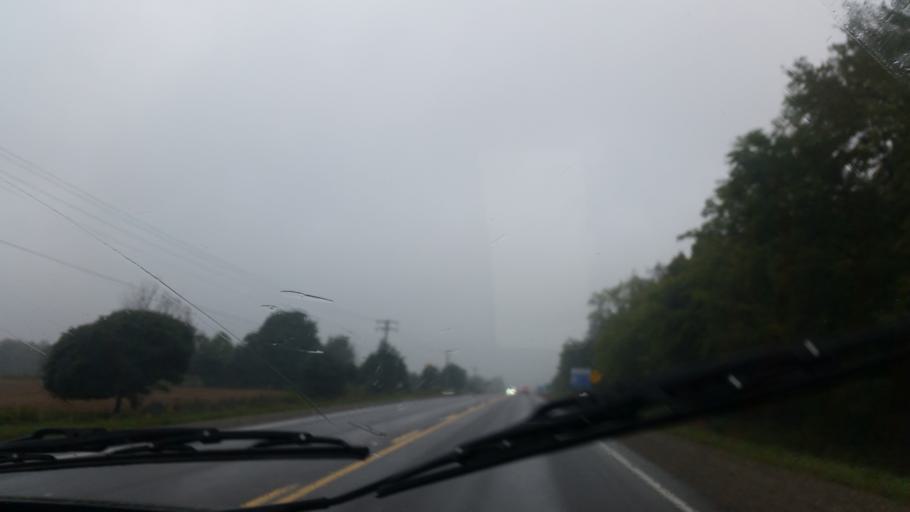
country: CA
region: Ontario
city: Stratford
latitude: 43.2748
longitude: -81.0641
